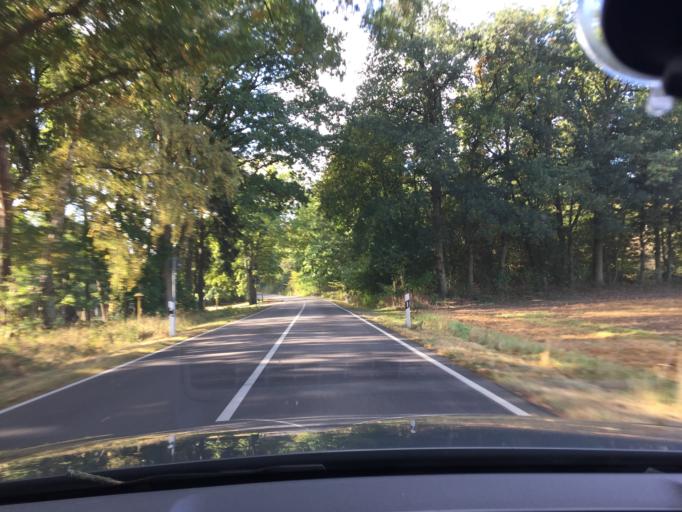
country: DE
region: Mecklenburg-Vorpommern
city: Krakow am See
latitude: 53.6711
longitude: 12.2740
